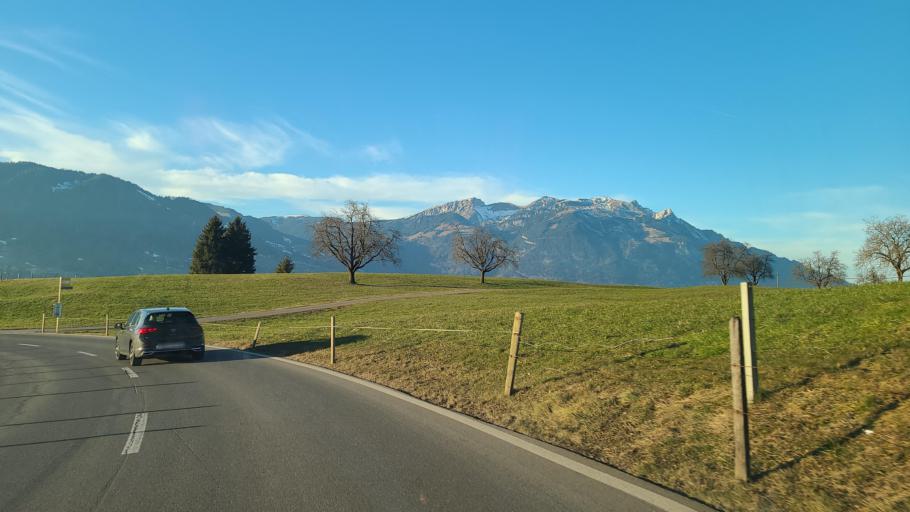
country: CH
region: Obwalden
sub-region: Obwalden
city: Kerns
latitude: 46.8889
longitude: 8.2778
